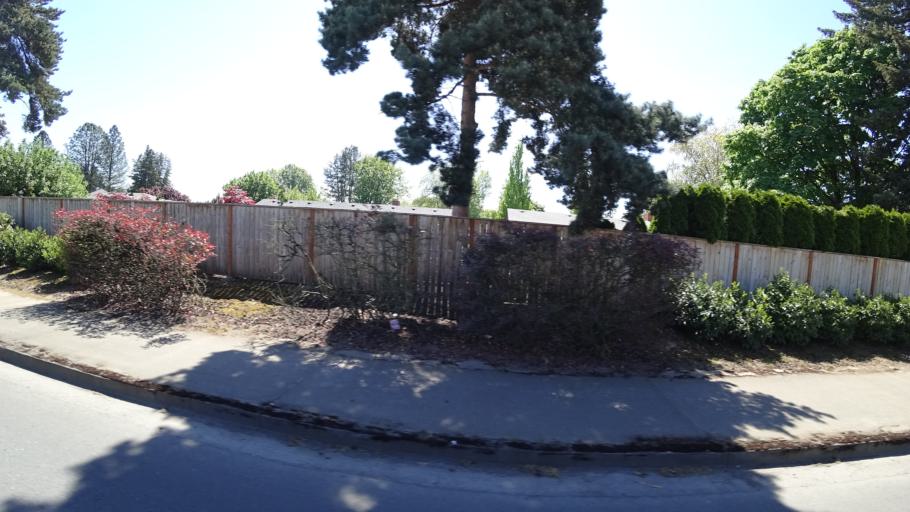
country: US
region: Oregon
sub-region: Washington County
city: Hillsboro
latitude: 45.5023
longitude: -122.9584
